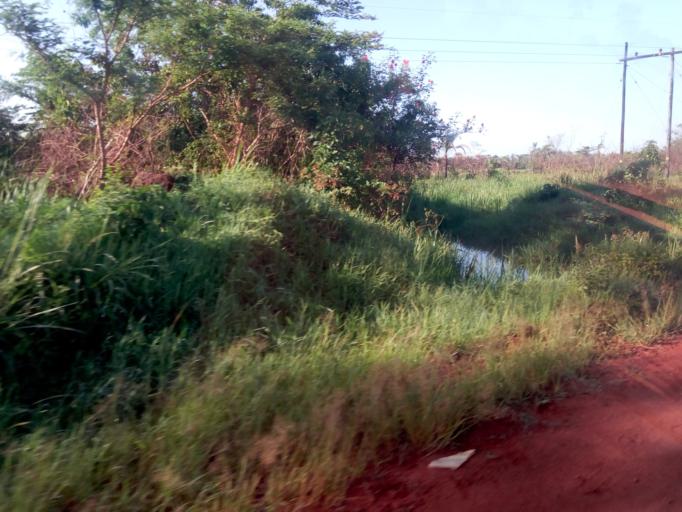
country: UG
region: Western Region
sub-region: Masindi District
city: Masindi
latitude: 1.7751
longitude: 31.8232
